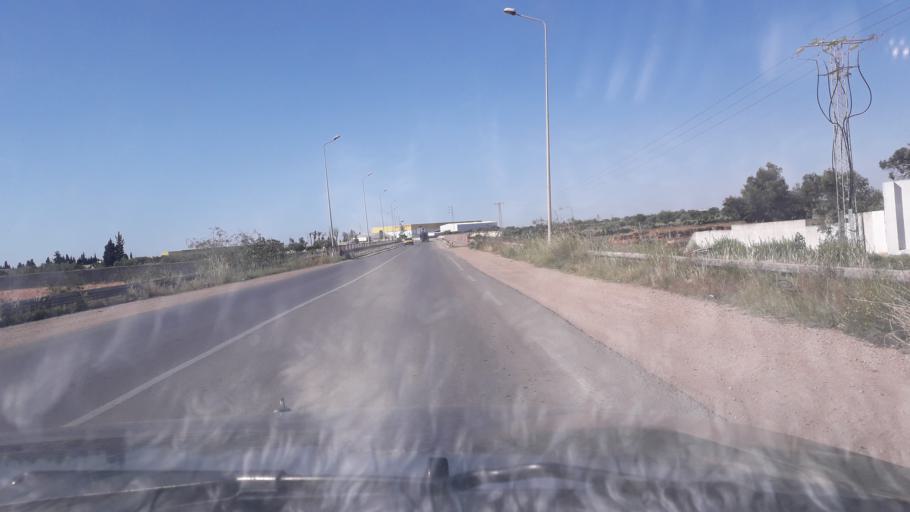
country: TN
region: Safaqis
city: Al Qarmadah
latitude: 34.8769
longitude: 10.7571
